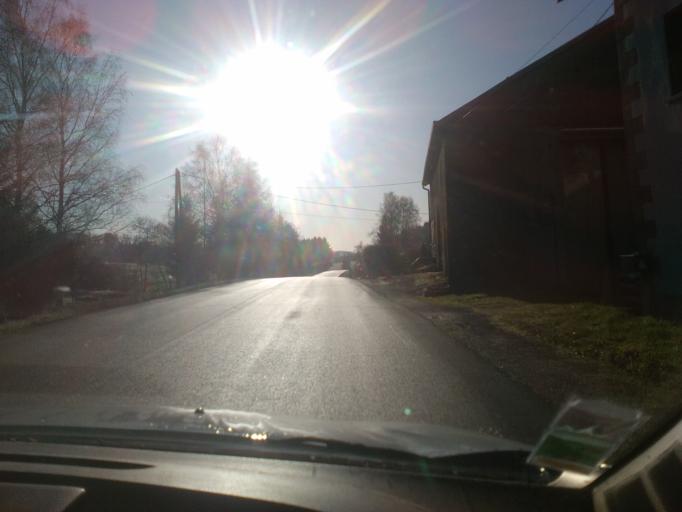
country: FR
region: Lorraine
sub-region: Departement des Vosges
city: Xertigny
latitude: 48.0156
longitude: 6.4253
